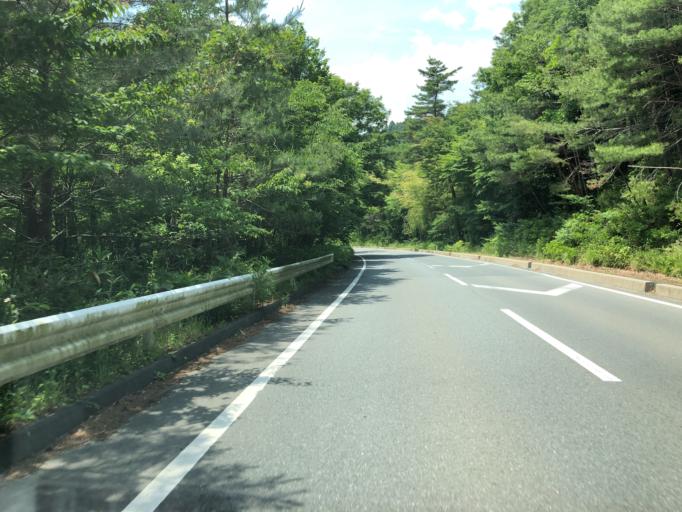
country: JP
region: Fukushima
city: Namie
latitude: 37.5885
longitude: 140.9353
